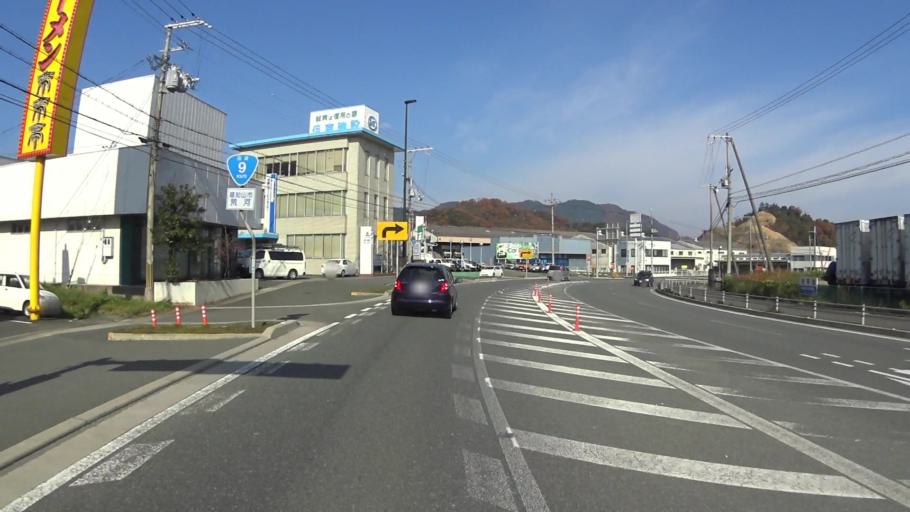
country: JP
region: Kyoto
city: Fukuchiyama
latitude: 35.3233
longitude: 135.0969
